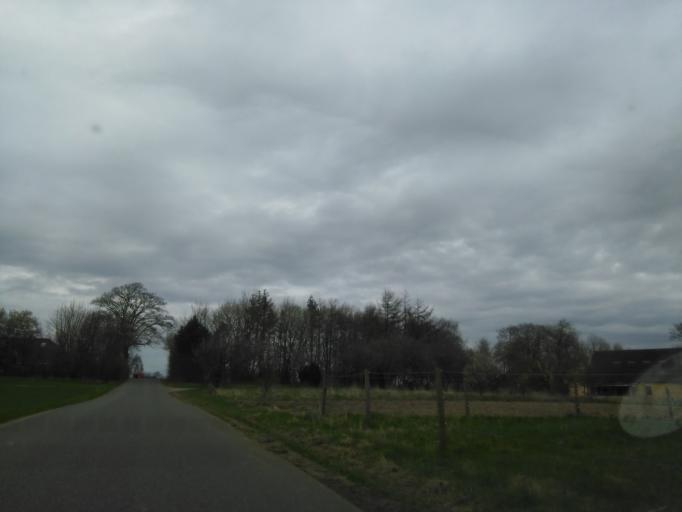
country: DK
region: Central Jutland
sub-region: Skanderborg Kommune
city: Stilling
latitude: 56.0761
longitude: 9.9954
